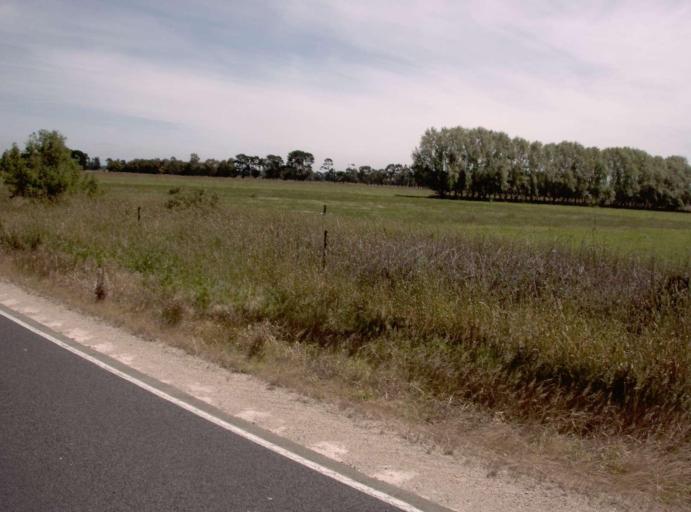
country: AU
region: Victoria
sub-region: Wellington
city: Heyfield
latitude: -38.0332
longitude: 146.8787
